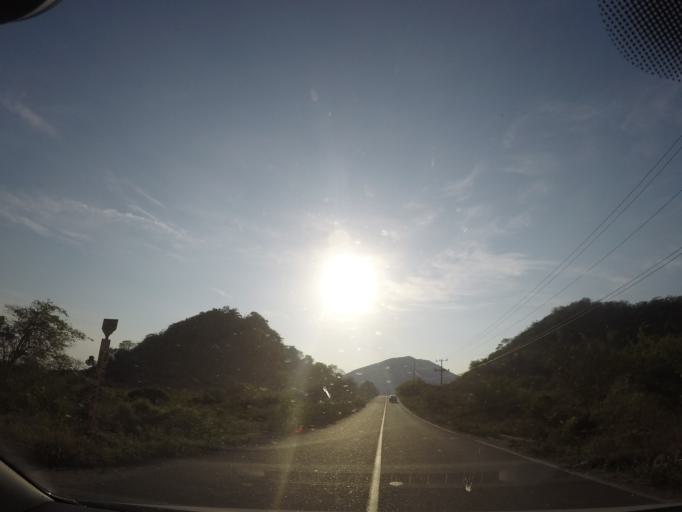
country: MX
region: Oaxaca
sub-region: Santo Domingo Tehuantepec
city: La Noria
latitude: 16.2360
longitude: -95.1662
